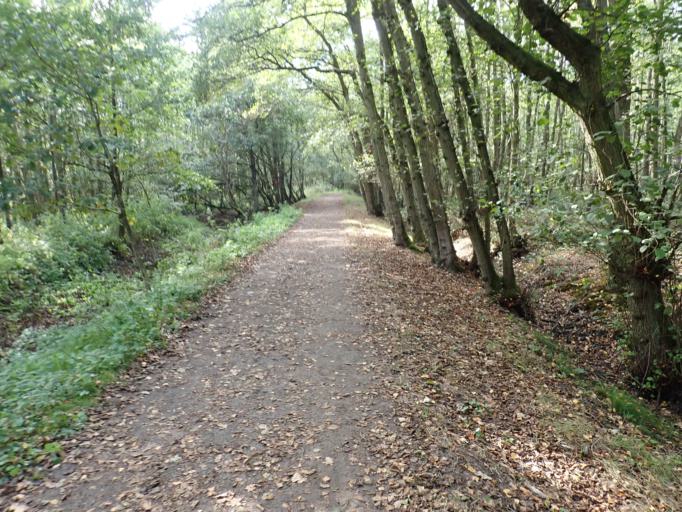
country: NL
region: Zeeland
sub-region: Gemeente Hulst
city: Hulst
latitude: 51.2400
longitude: 4.0724
